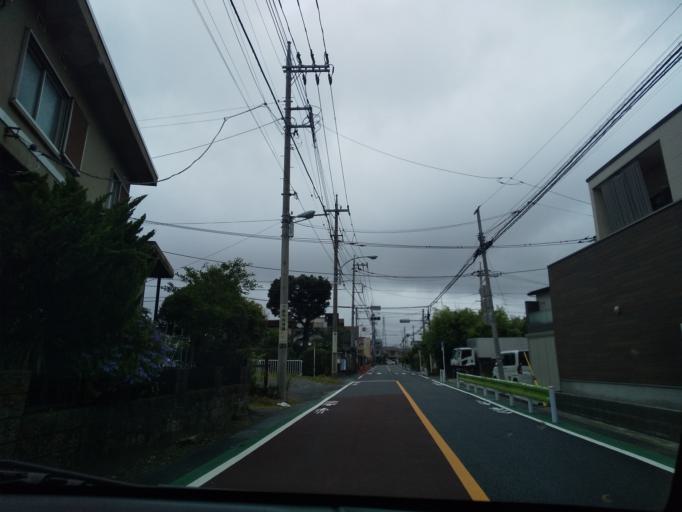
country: JP
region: Tokyo
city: Hino
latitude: 35.6764
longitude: 139.4161
